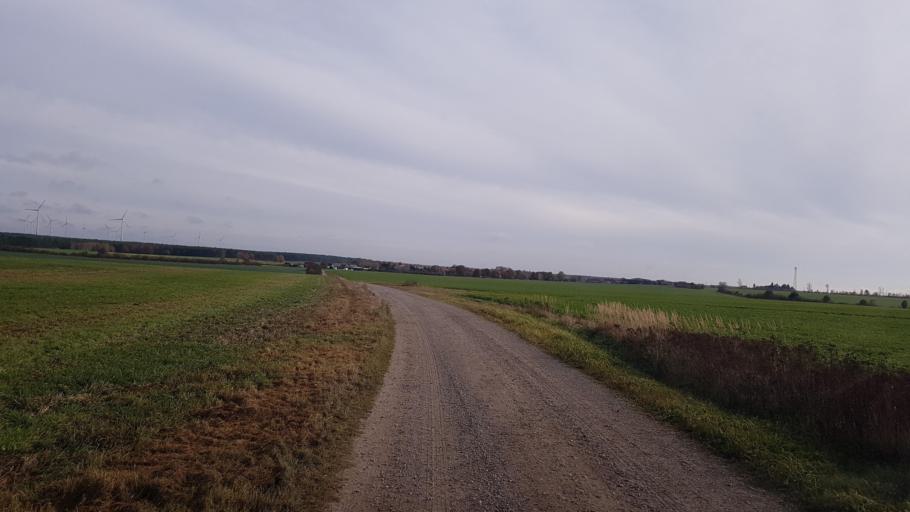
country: DE
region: Brandenburg
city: Niedergorsdorf
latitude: 52.0146
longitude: 12.9044
